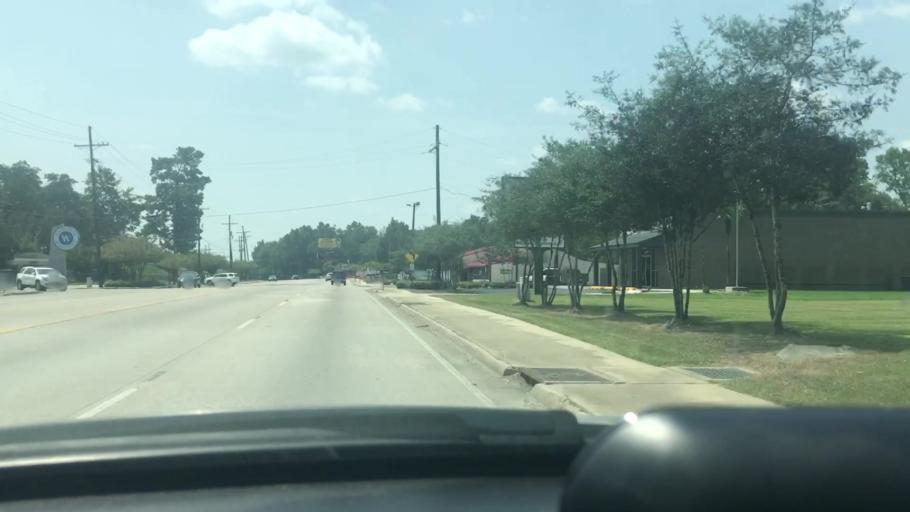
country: US
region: Louisiana
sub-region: Livingston Parish
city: Walker
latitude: 30.4857
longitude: -90.8624
